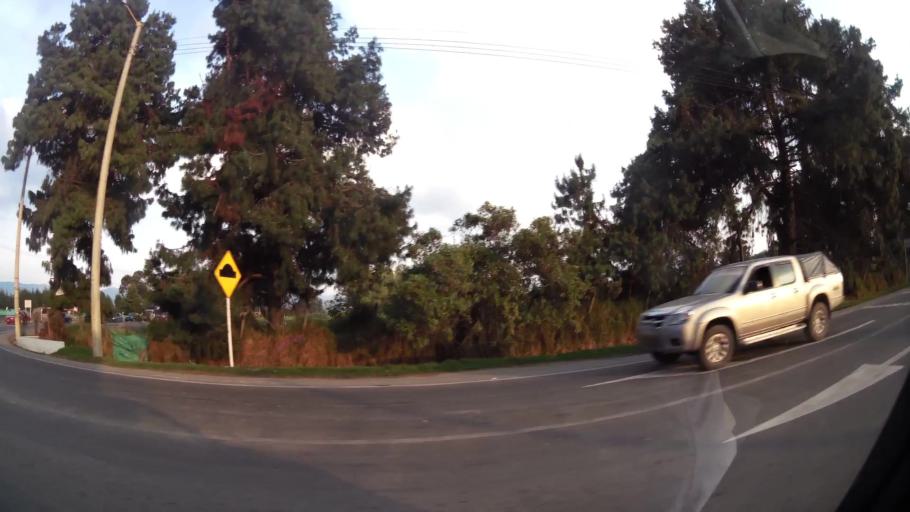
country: CO
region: Cundinamarca
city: Cota
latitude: 4.7991
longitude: -74.1109
